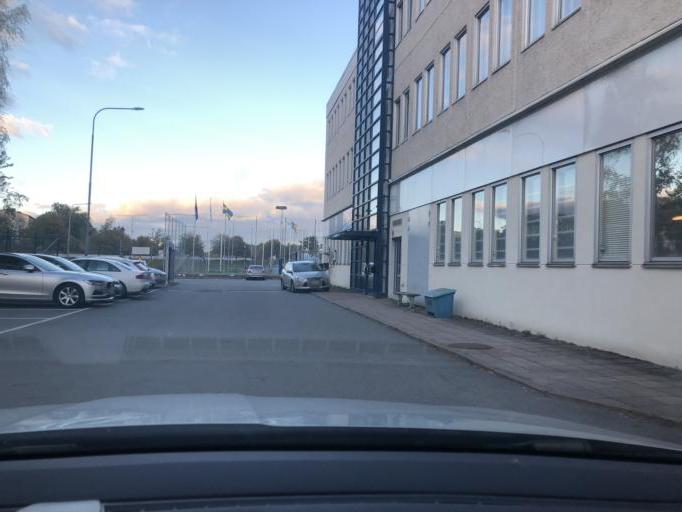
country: SE
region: Stockholm
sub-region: Huddinge Kommun
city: Segeltorp
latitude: 59.2806
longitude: 17.9173
